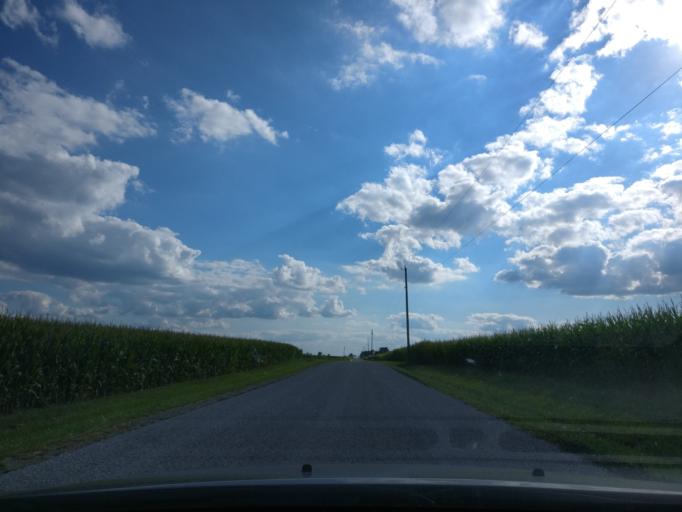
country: US
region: Ohio
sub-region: Clinton County
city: Wilmington
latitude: 39.5251
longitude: -83.7719
